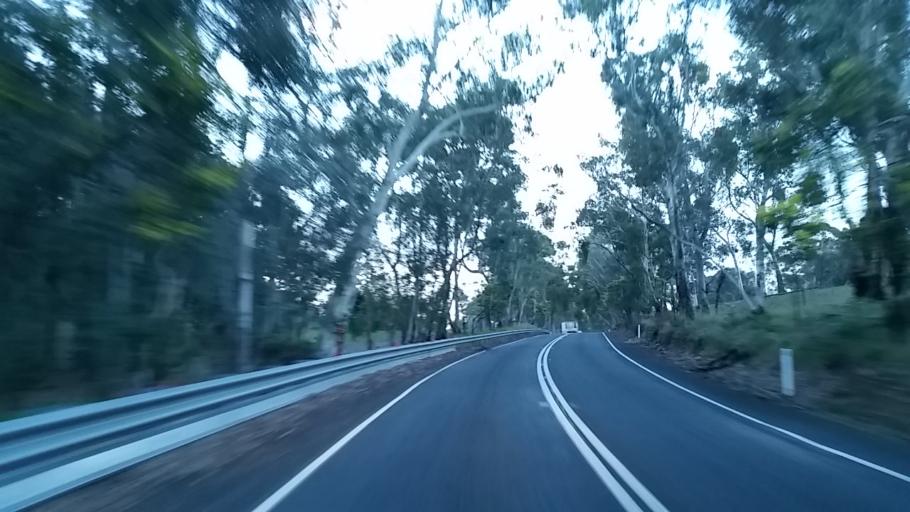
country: AU
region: South Australia
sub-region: Barossa
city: Williamstown
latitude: -34.6956
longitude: 138.8791
